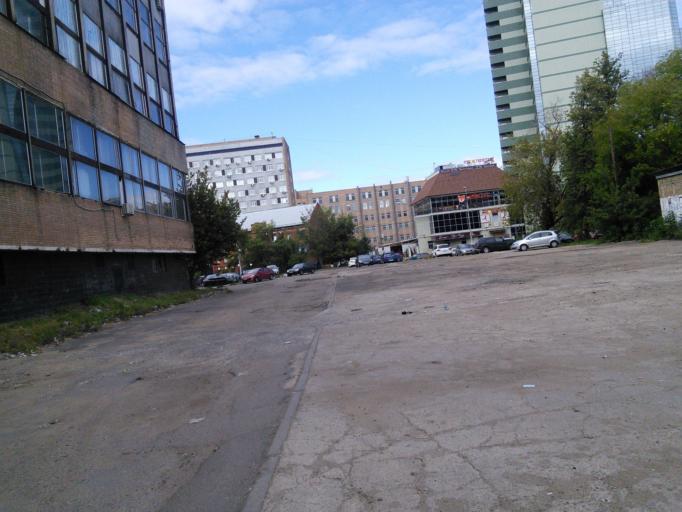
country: RU
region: Moscow
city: Lefortovo
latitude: 55.7814
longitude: 37.7168
